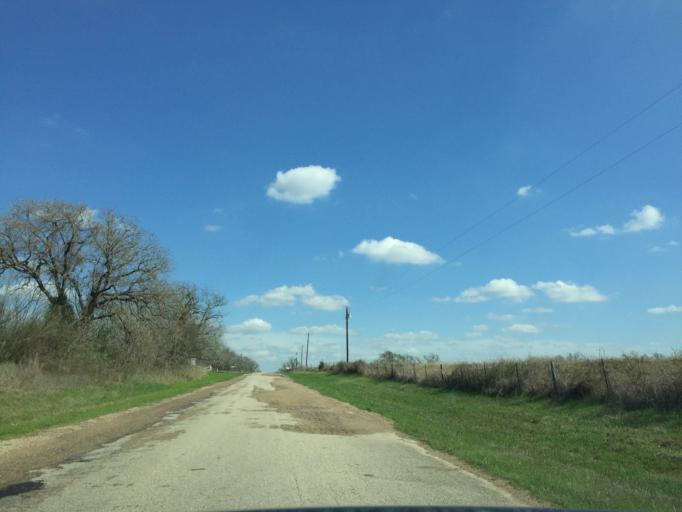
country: US
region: Texas
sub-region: Milam County
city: Thorndale
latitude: 30.5578
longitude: -97.1696
